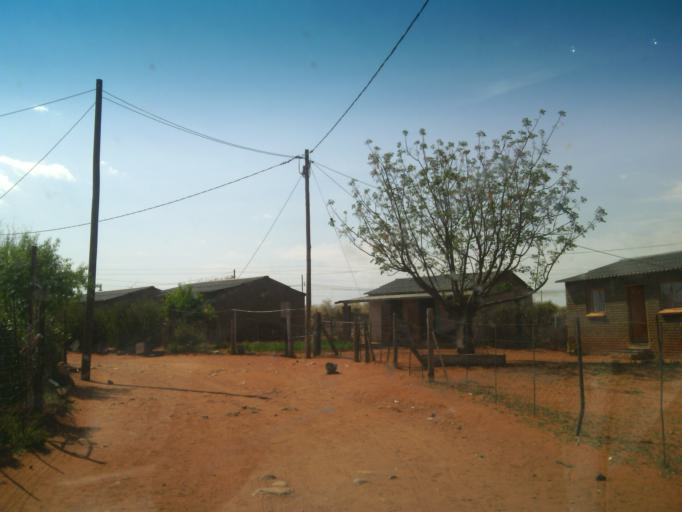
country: ZA
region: Northern Cape
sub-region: Frances Baard District Municipality
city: Barkly West
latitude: -28.5184
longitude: 24.5039
